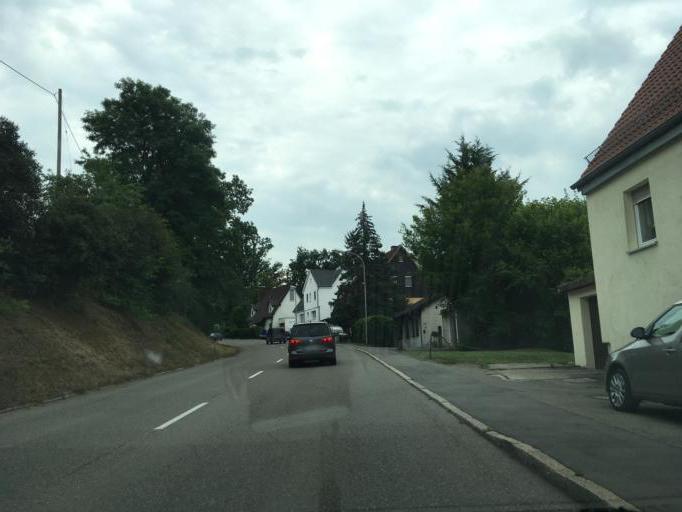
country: DE
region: Baden-Wuerttemberg
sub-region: Tuebingen Region
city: Dettenhausen
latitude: 48.6074
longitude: 9.1037
